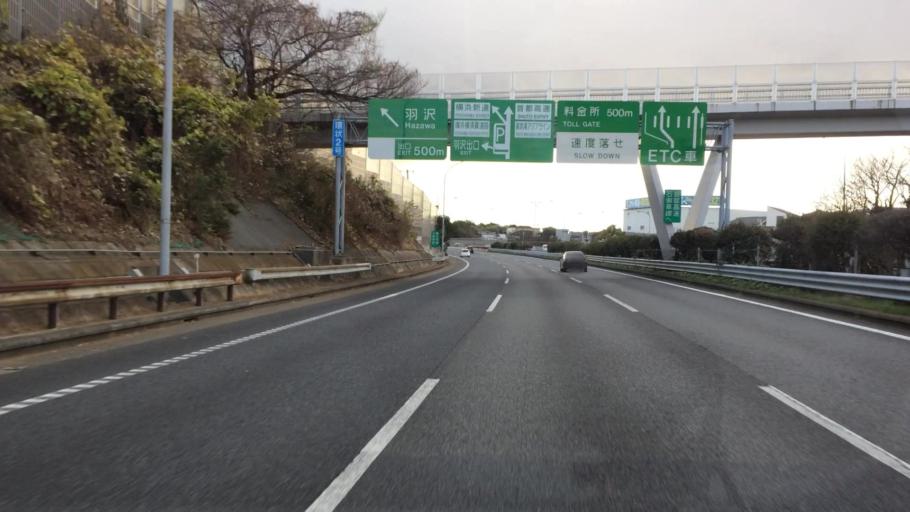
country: JP
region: Kanagawa
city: Yokohama
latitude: 35.4891
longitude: 139.5923
